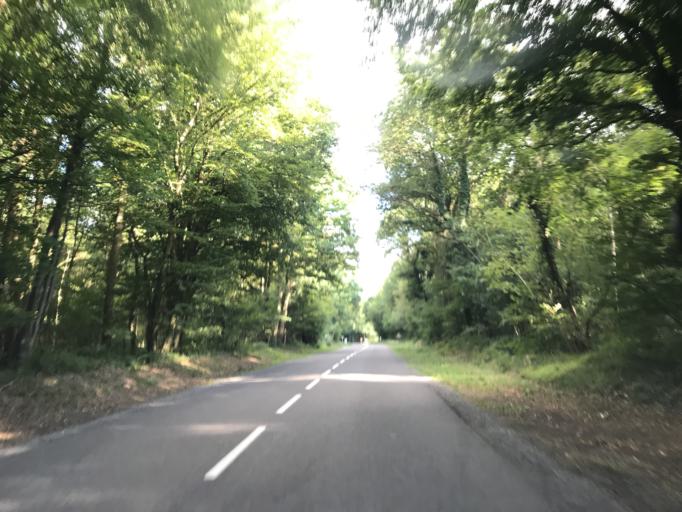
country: FR
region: Haute-Normandie
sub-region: Departement de l'Eure
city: Courcelles-sur-Seine
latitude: 49.1820
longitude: 1.3865
